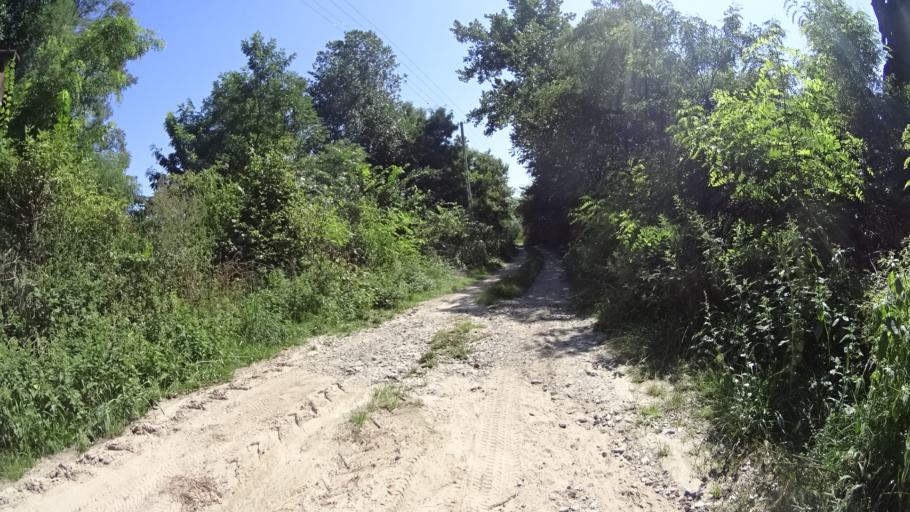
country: PL
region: Masovian Voivodeship
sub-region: Powiat grojecki
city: Goszczyn
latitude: 51.6649
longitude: 20.8748
